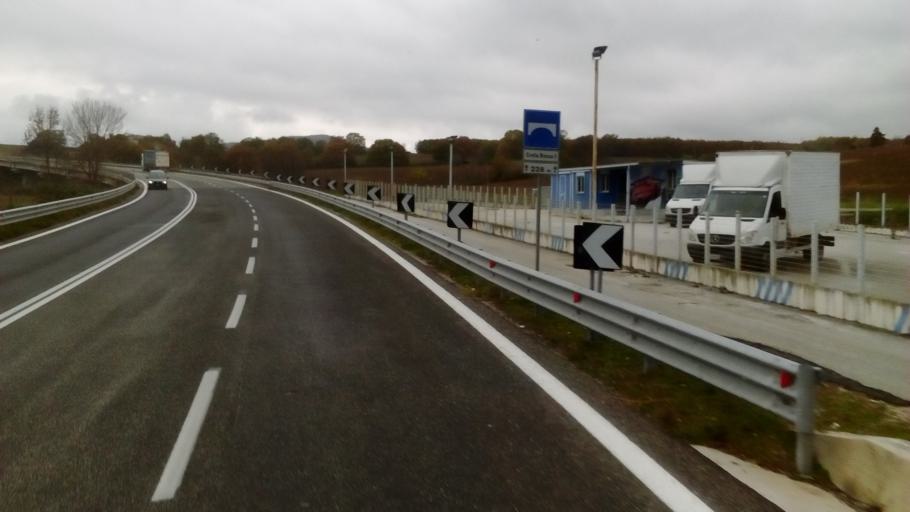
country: IT
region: Molise
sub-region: Provincia di Isernia
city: Bagnoli del Trigno
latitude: 41.7180
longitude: 14.4254
